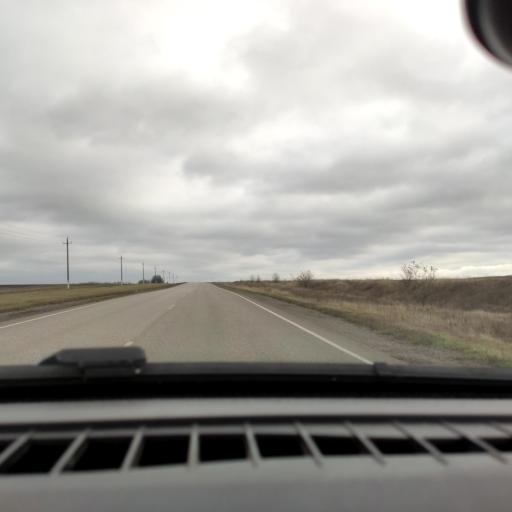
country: RU
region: Belgorod
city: Ilovka
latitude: 50.7700
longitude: 38.7661
